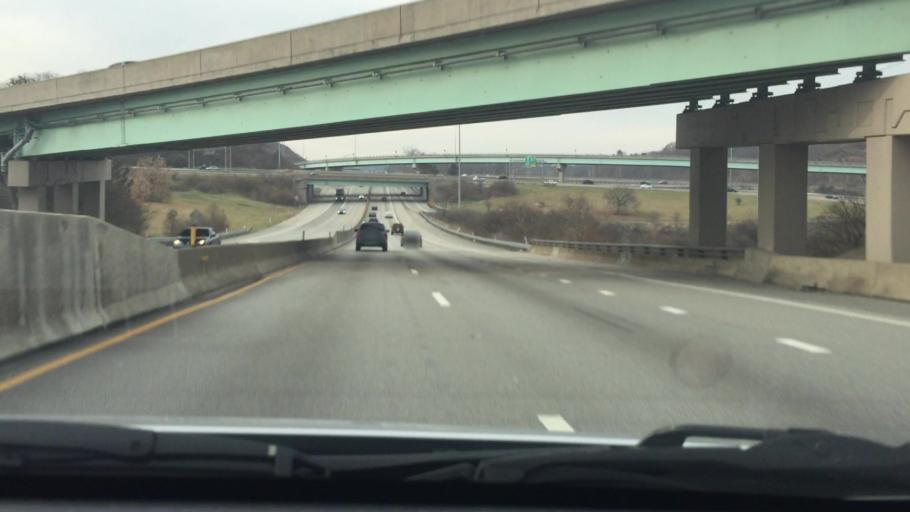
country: US
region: Pennsylvania
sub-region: Allegheny County
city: Carnegie
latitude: 40.4228
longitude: -80.1022
